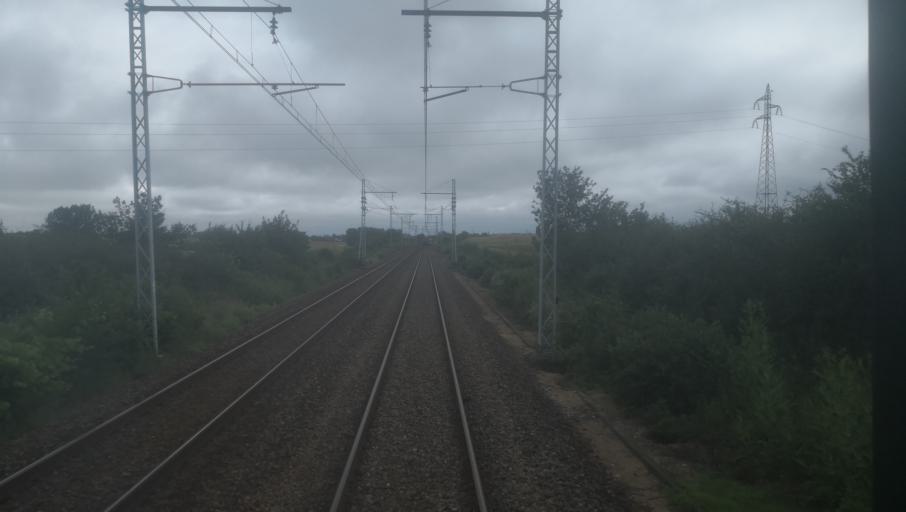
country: FR
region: Centre
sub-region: Departement de l'Indre
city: Saint-Maur
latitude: 46.7861
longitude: 1.6484
